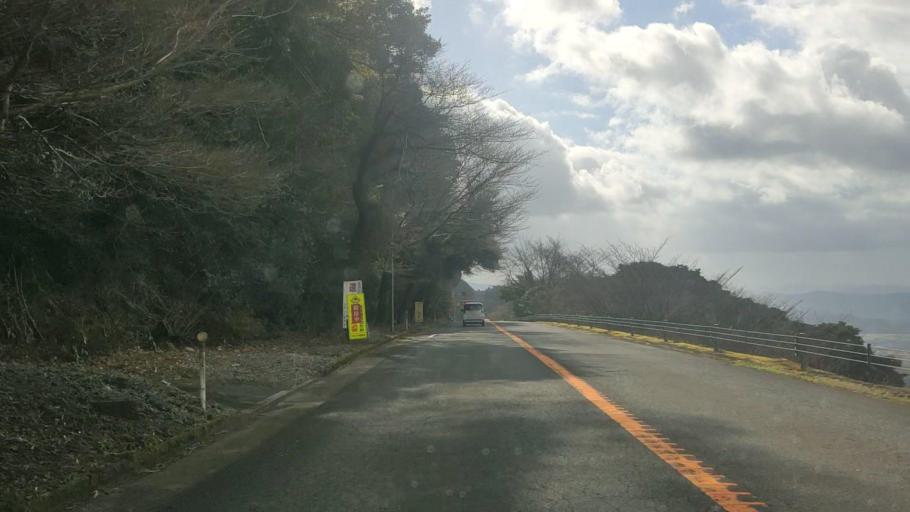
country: JP
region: Kumamoto
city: Hitoyoshi
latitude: 32.0880
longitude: 130.8015
